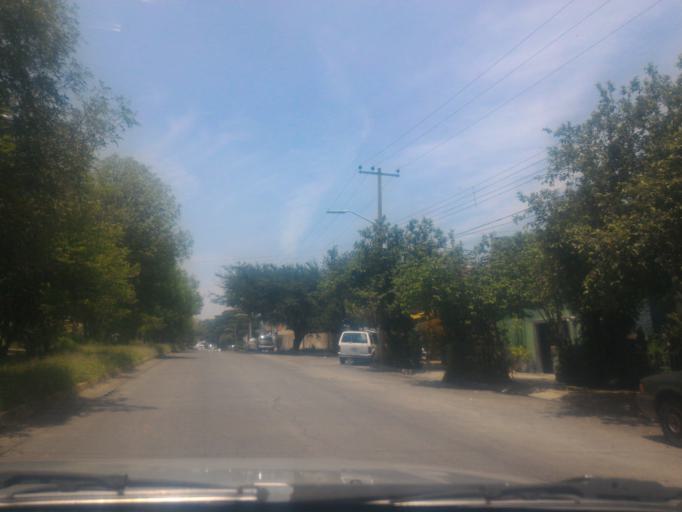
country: MX
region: Jalisco
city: Las Pintas de Arriba
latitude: 20.6205
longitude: -103.3508
